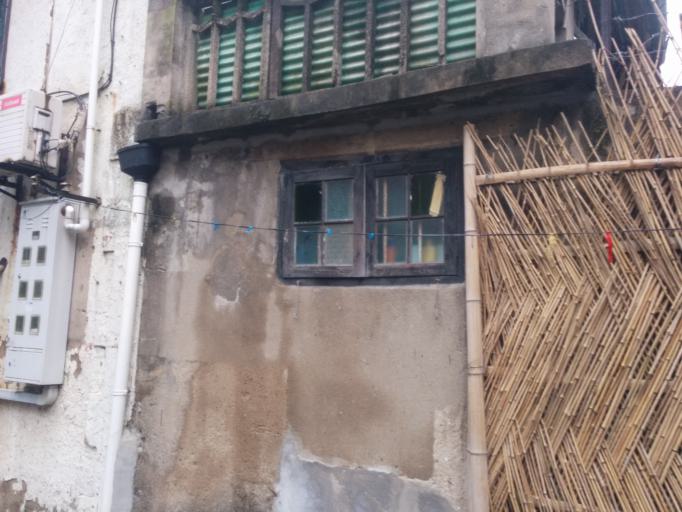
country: CN
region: Shanghai Shi
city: Shanghai
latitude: 31.2209
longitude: 121.4432
